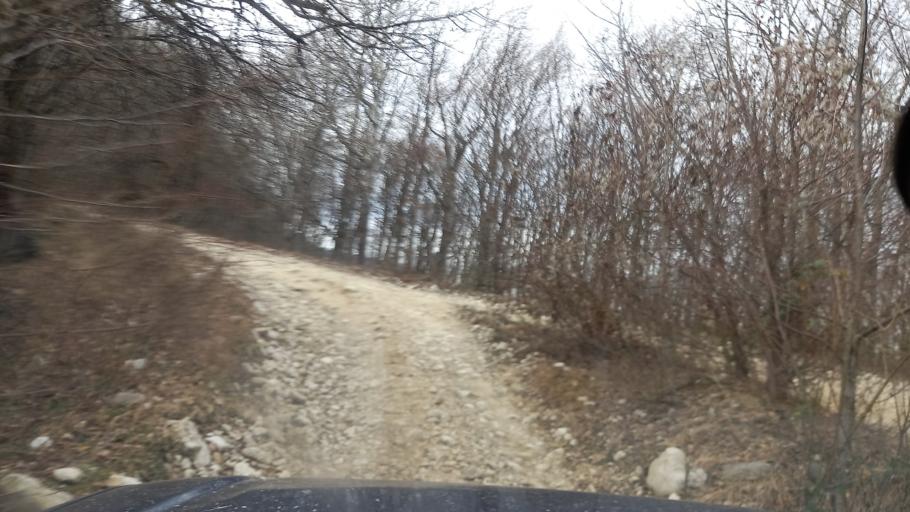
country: RU
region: Krasnodarskiy
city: Neftegorsk
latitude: 44.2223
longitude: 39.8962
